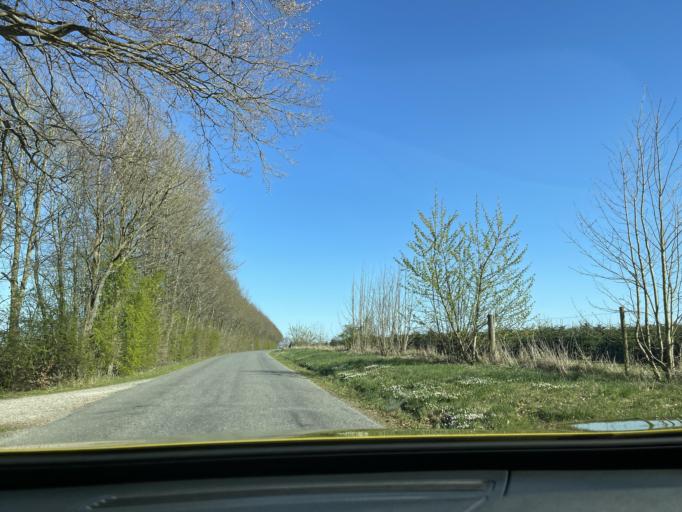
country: DK
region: Central Jutland
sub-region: Silkeborg Kommune
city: Kjellerup
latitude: 56.2465
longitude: 9.4796
